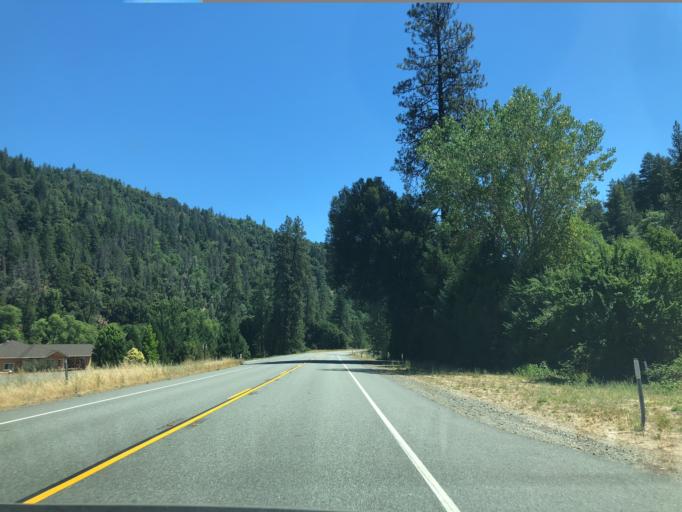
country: US
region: California
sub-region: Trinity County
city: Weaverville
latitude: 40.6562
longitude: -122.9229
